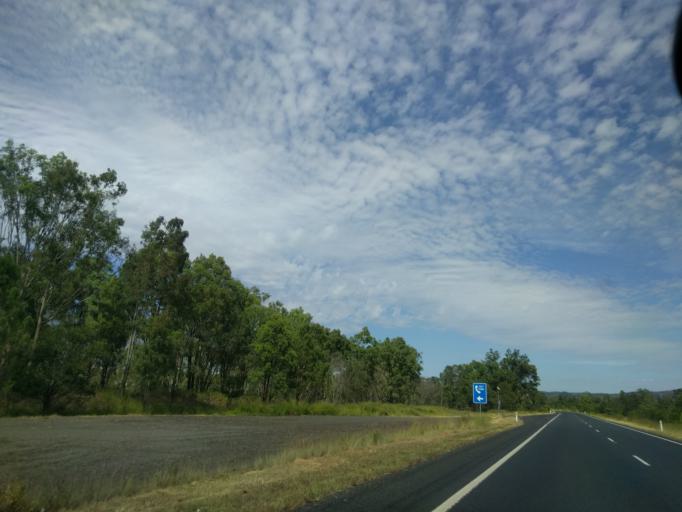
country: AU
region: Queensland
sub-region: Lockyer Valley
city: Gatton
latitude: -27.5356
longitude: 152.2611
